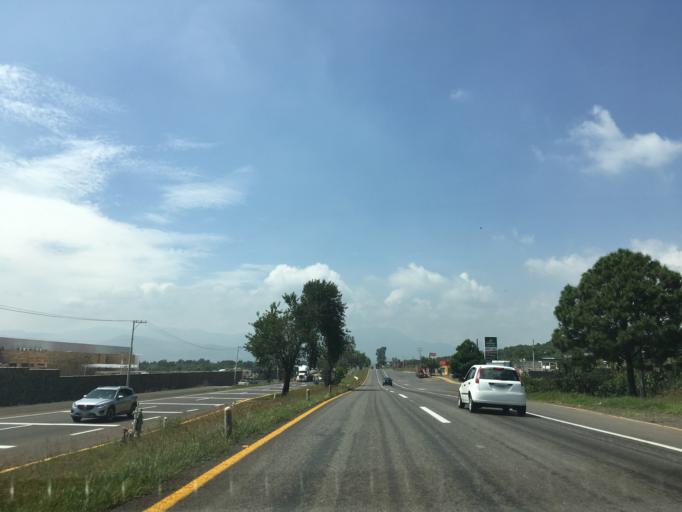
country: MX
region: Michoacan
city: Acuitzio del Canje
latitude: 19.5751
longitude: -101.3155
